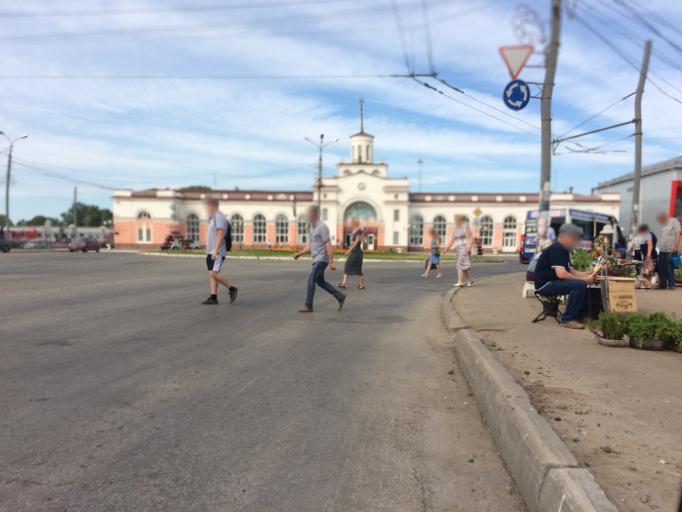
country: RU
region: Mariy-El
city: Yoshkar-Ola
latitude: 56.6224
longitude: 47.8815
